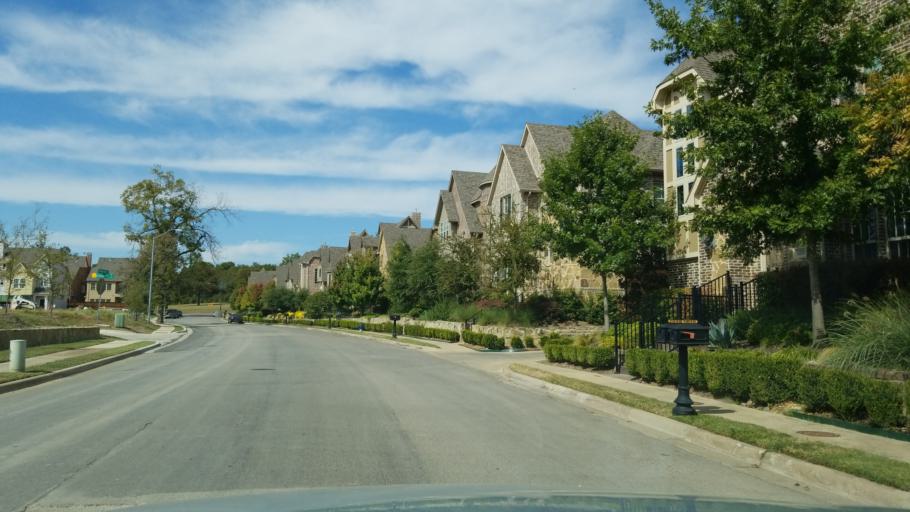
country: US
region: Texas
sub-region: Dallas County
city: Highland Park
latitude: 32.8076
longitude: -96.7351
